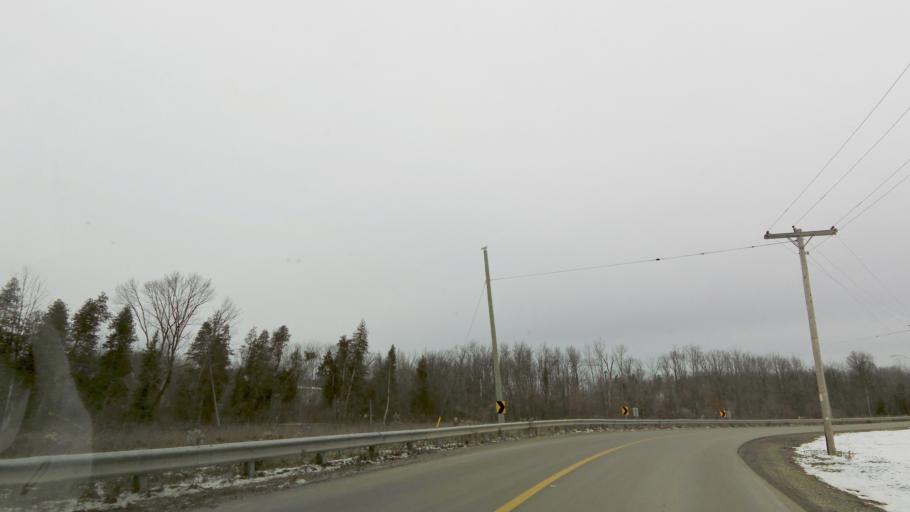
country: CA
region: Ontario
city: Bradford West Gwillimbury
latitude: 44.0777
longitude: -79.5852
